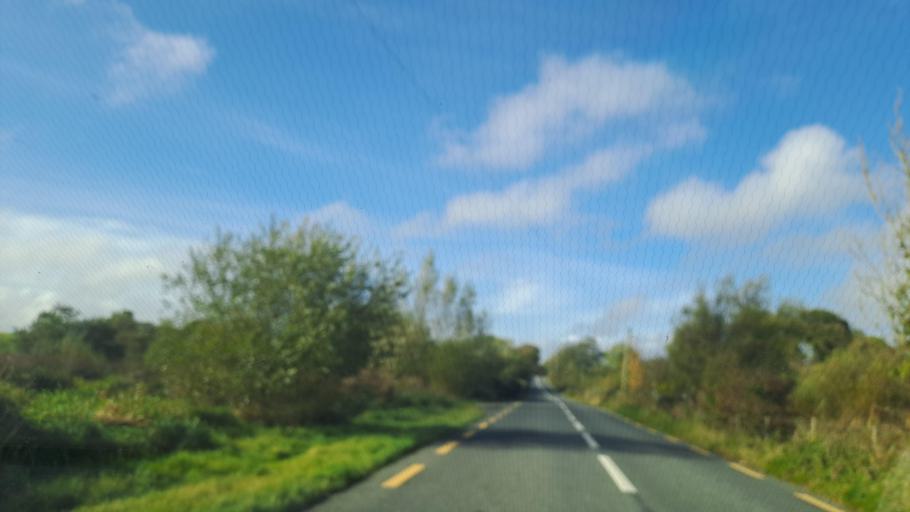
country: IE
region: Ulster
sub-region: An Cabhan
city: Cootehill
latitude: 54.0576
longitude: -7.0225
